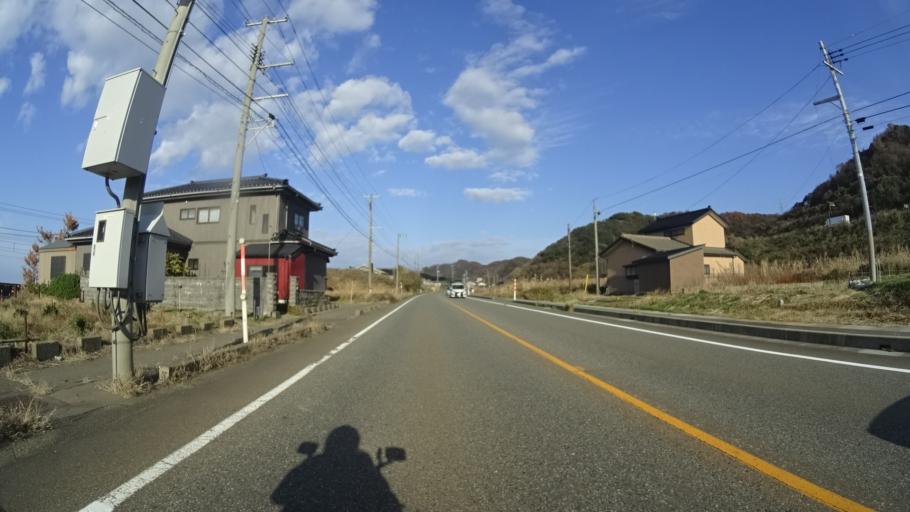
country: JP
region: Niigata
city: Kashiwazaki
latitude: 37.3125
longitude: 138.4264
